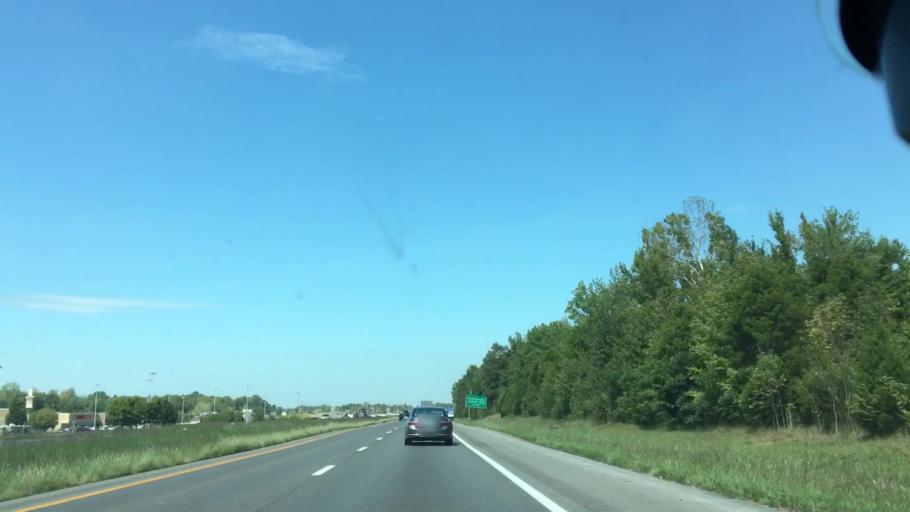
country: US
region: Kentucky
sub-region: Hopkins County
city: Madisonville
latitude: 37.3160
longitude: -87.4720
